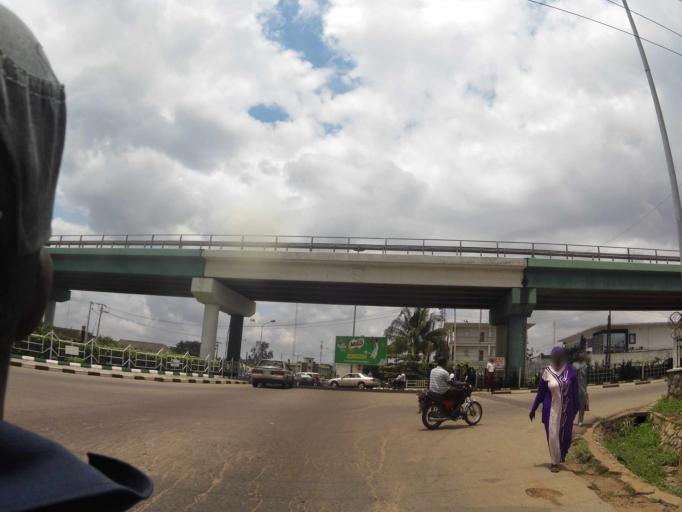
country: NG
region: Oyo
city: Ibadan
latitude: 7.4074
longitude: 3.9110
